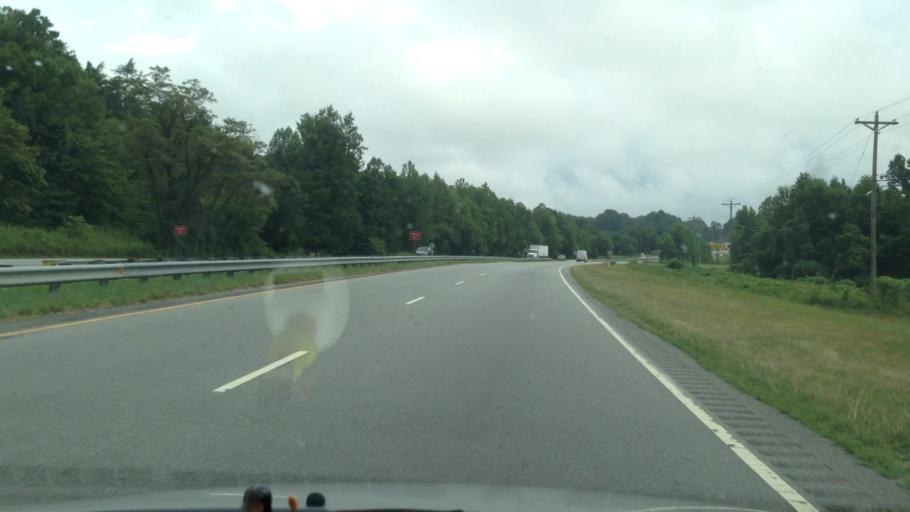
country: US
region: North Carolina
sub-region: Rockingham County
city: Madison
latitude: 36.3259
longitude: -79.9462
